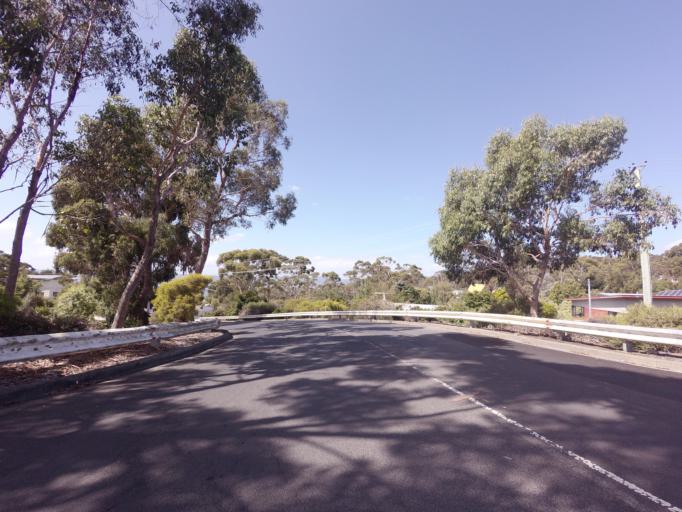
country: AU
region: Tasmania
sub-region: Hobart
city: Dynnyrne
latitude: -42.9202
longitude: 147.3227
